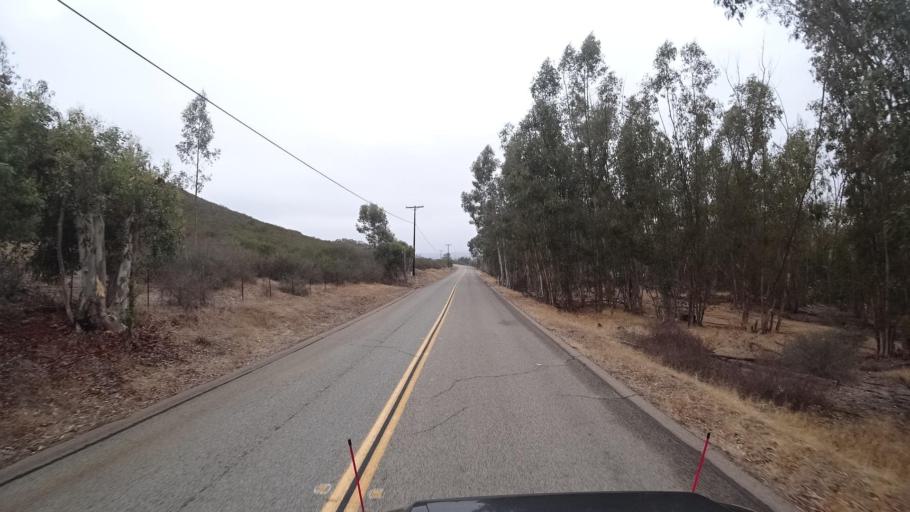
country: US
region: California
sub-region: San Diego County
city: Poway
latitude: 32.9420
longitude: -116.9976
